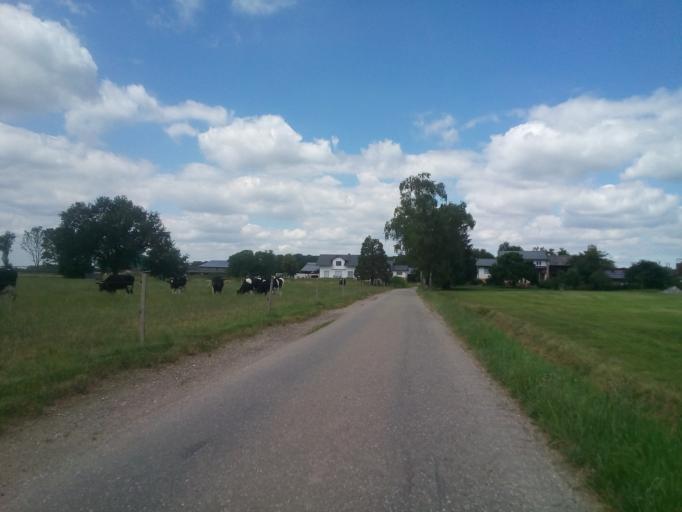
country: DE
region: Baden-Wuerttemberg
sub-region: Freiburg Region
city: Renchen
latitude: 48.6206
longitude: 7.9765
